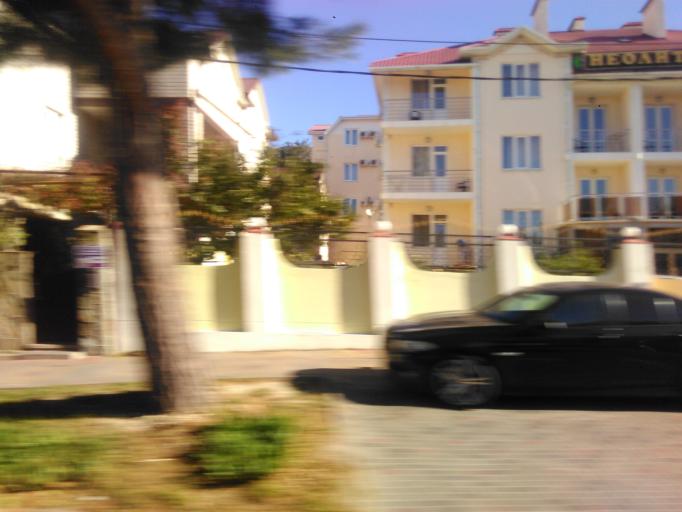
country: RU
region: Krasnodarskiy
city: Gelendzhik
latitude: 44.5832
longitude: 38.0612
